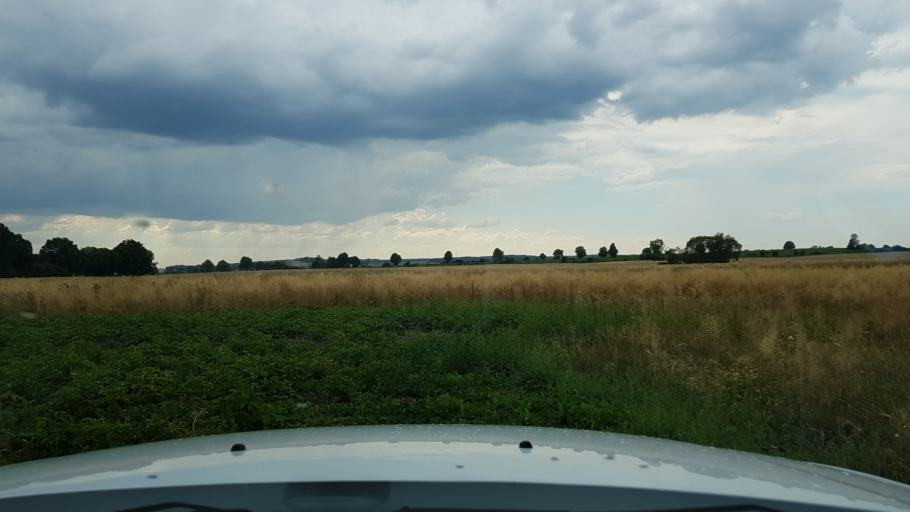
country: PL
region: West Pomeranian Voivodeship
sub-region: Powiat walecki
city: Walcz
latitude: 53.3563
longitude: 16.3589
